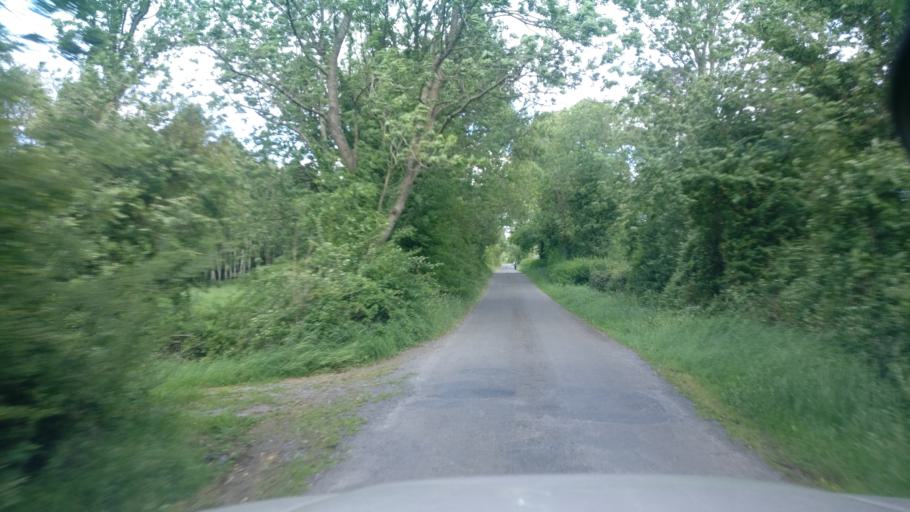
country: IE
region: Connaught
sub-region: County Galway
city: Portumna
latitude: 53.1997
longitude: -8.3338
